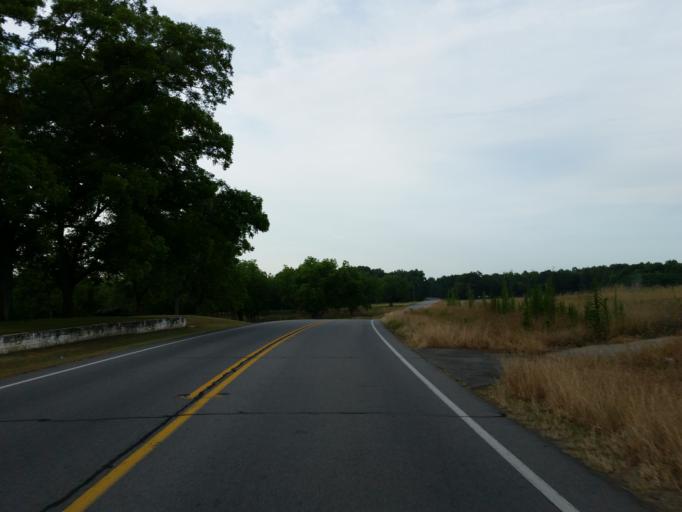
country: US
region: Georgia
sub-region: Dooly County
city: Unadilla
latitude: 32.2179
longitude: -83.7592
